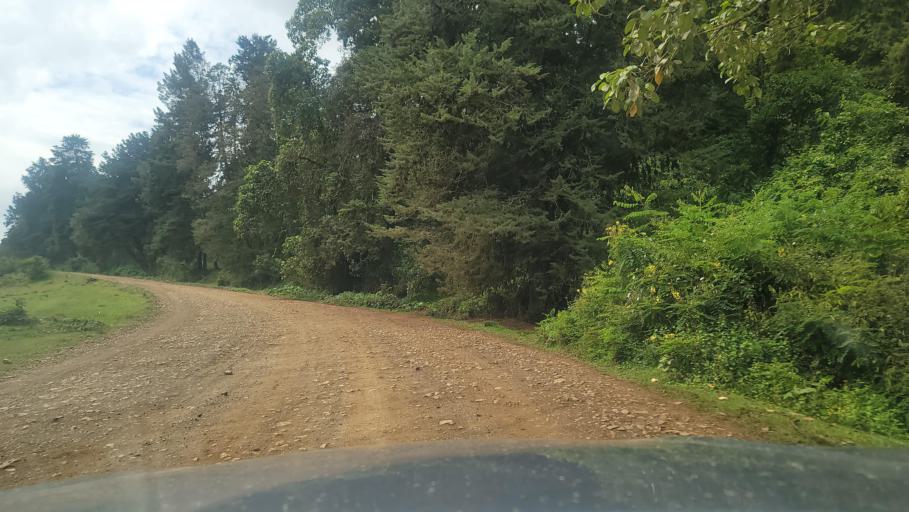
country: ET
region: Oromiya
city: Agaro
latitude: 7.7909
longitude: 36.4313
